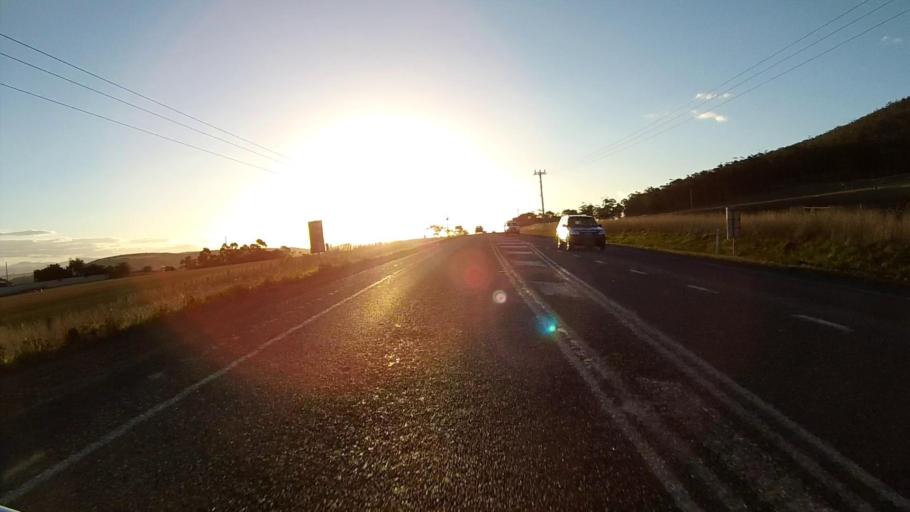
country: AU
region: Tasmania
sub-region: Sorell
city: Sorell
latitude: -42.7982
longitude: 147.6133
